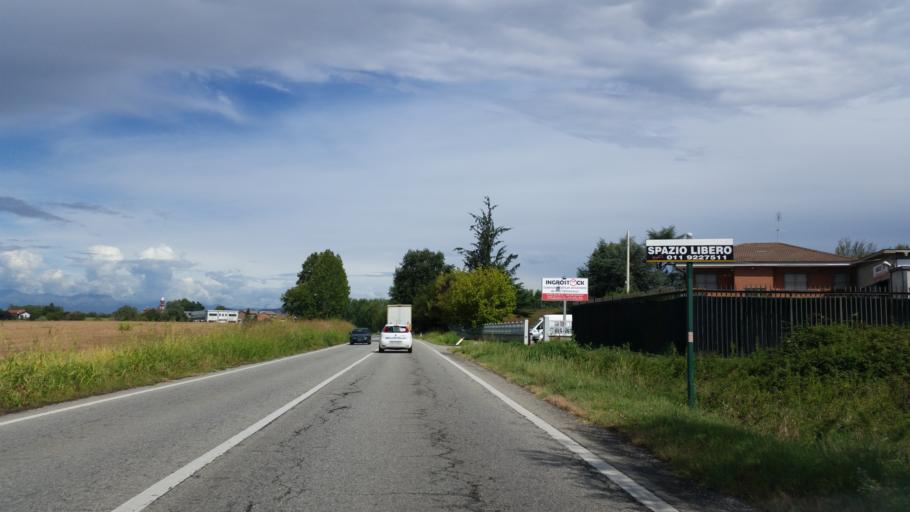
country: IT
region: Piedmont
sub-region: Provincia di Torino
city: Marocchi
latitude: 44.9337
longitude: 7.8304
